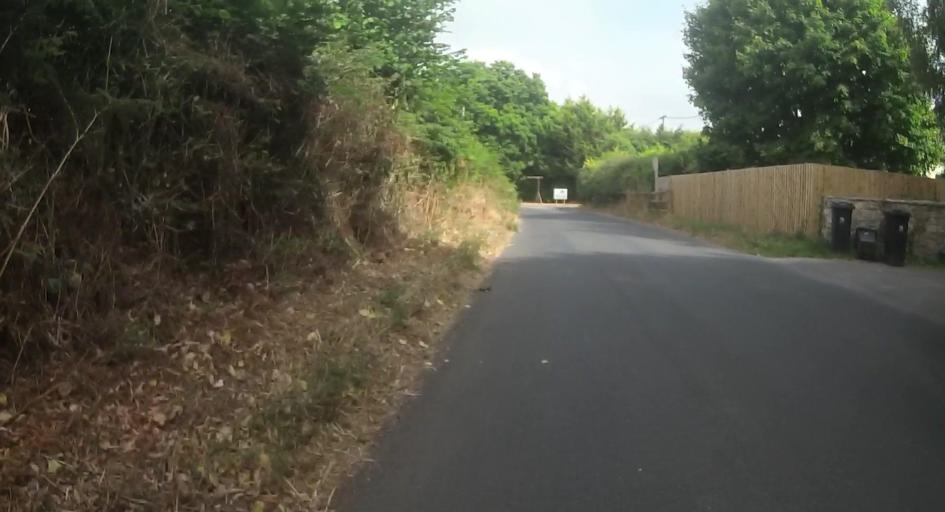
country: GB
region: England
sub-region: Dorset
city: Wool
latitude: 50.6748
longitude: -2.1910
